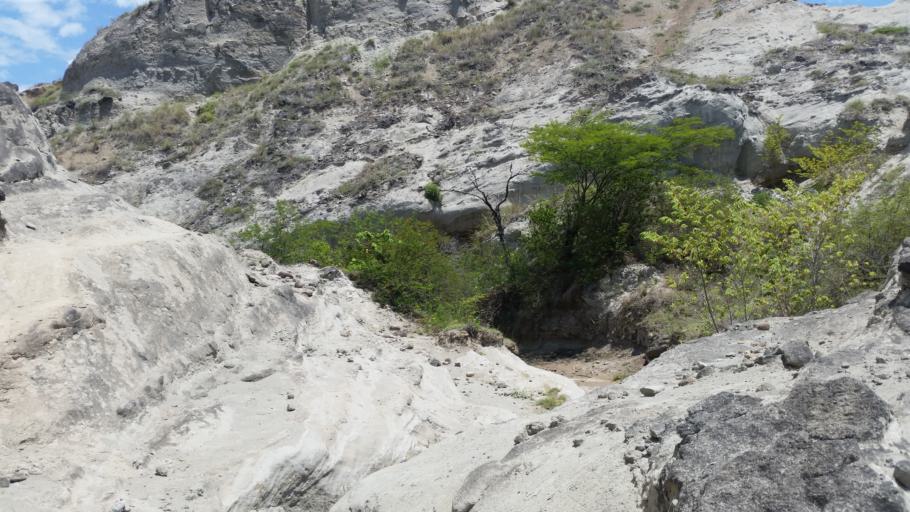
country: CO
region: Huila
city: Baraya
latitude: 3.2410
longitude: -75.1007
